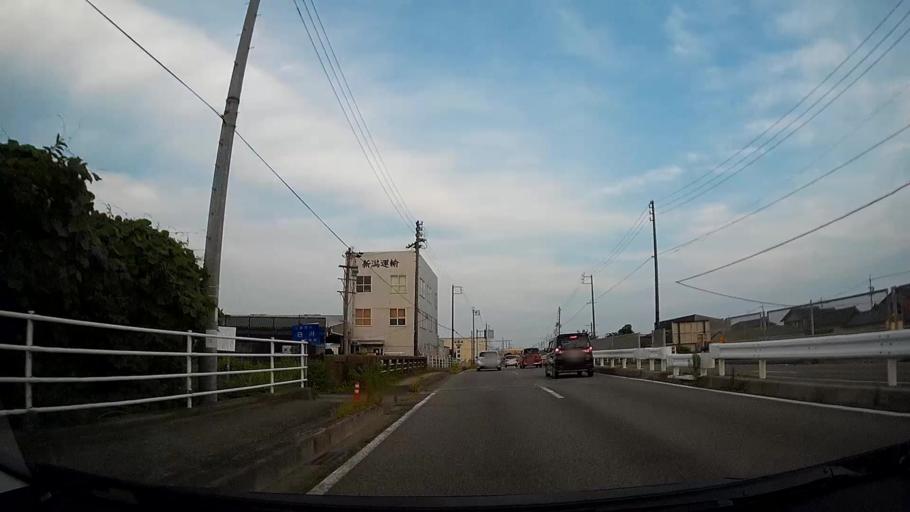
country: JP
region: Aichi
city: Kozakai-cho
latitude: 34.8193
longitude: 137.3474
